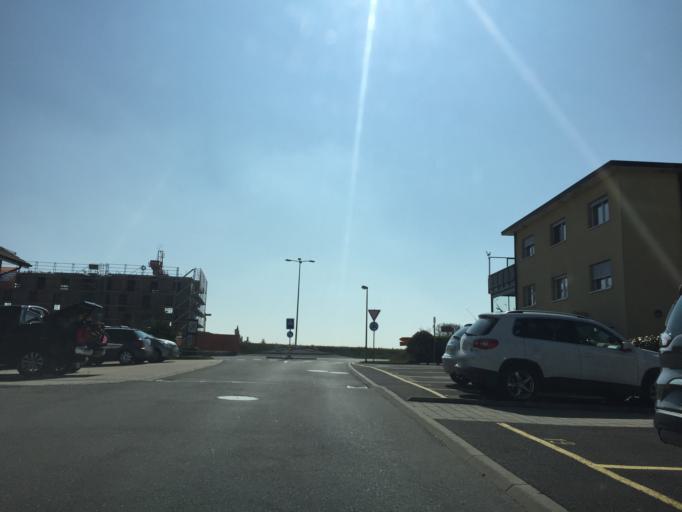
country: CH
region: Vaud
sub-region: Morges District
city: Cossonay
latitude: 46.6153
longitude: 6.5023
